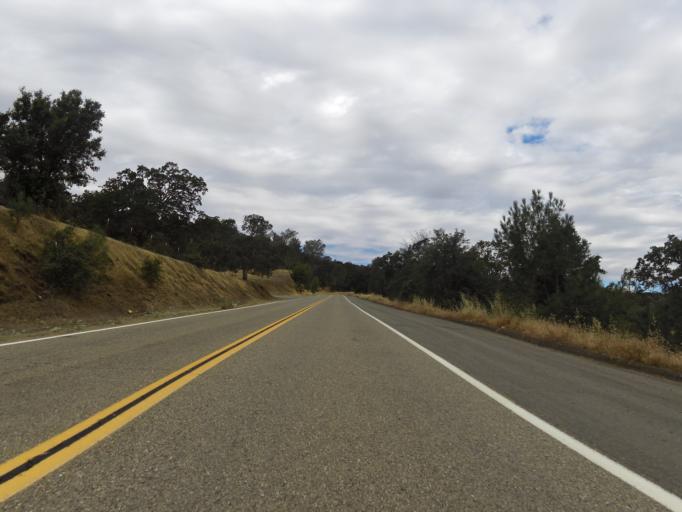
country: US
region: California
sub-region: Madera County
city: Yosemite Lakes
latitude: 37.2393
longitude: -119.7893
